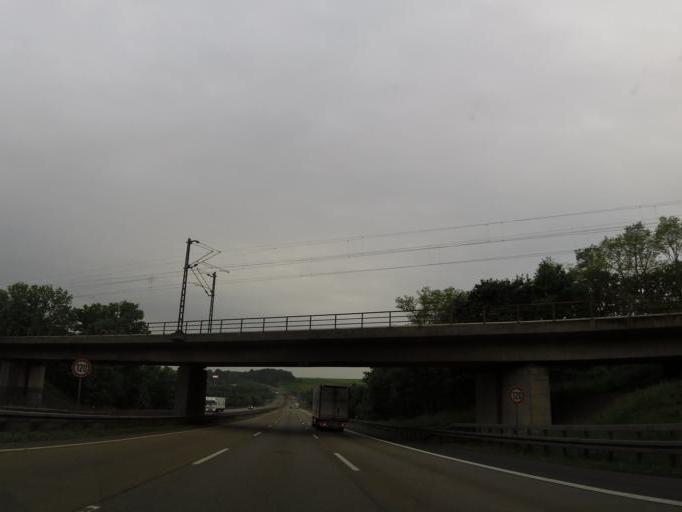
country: DE
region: Hesse
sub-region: Regierungsbezirk Kassel
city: Guxhagen
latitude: 51.2114
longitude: 9.4717
